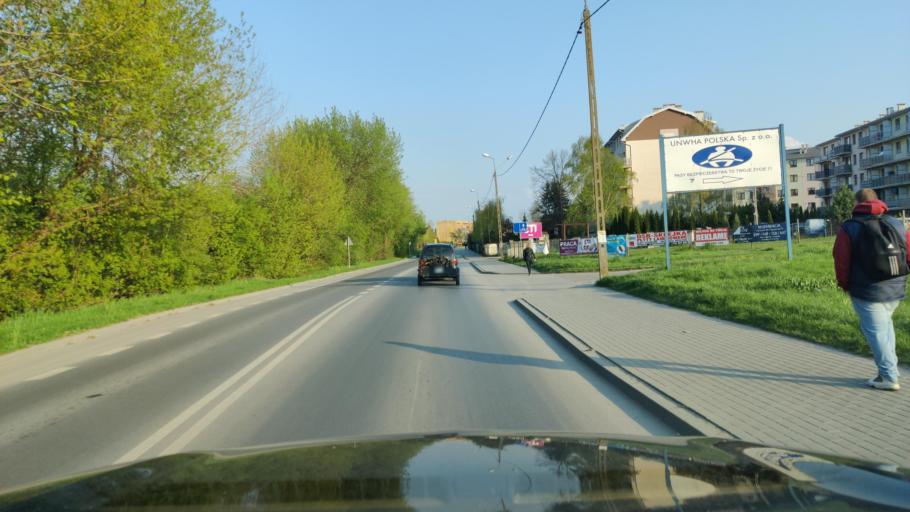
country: PL
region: Masovian Voivodeship
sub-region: Powiat pultuski
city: Pultusk
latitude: 52.6998
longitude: 21.0777
